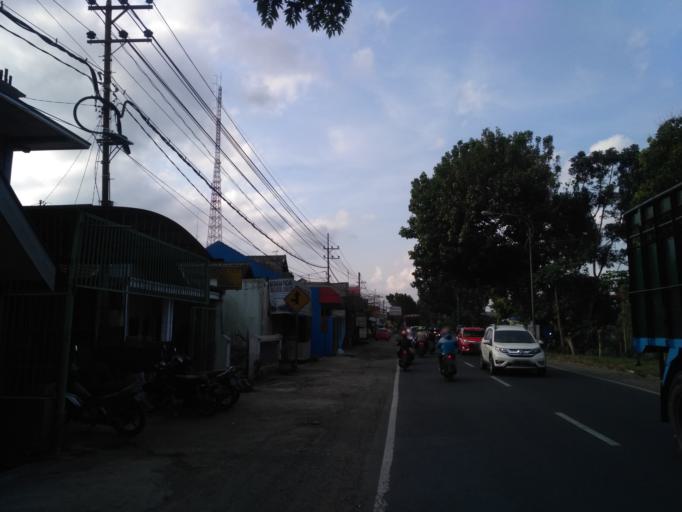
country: ID
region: East Java
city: Wadung
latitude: -8.0459
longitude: 112.6075
